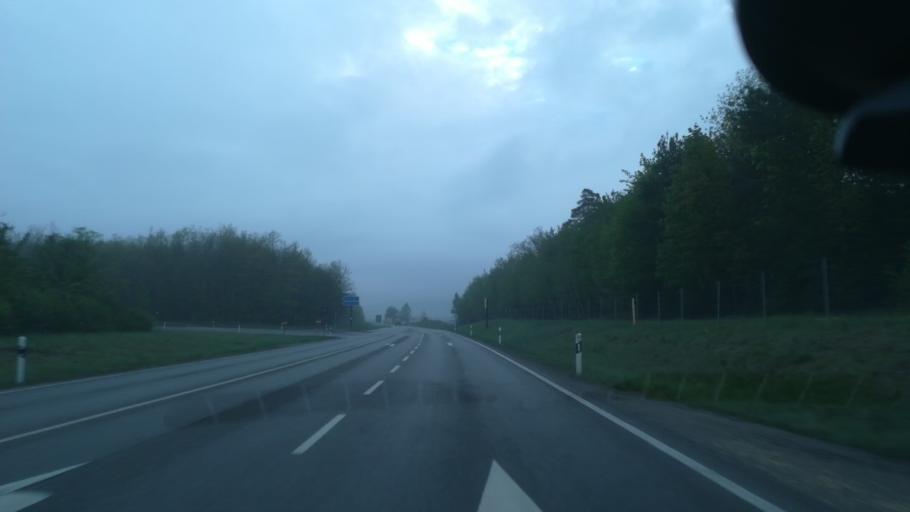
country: DE
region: Baden-Wuerttemberg
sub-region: Freiburg Region
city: Steisslingen
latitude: 47.7706
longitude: 8.9145
